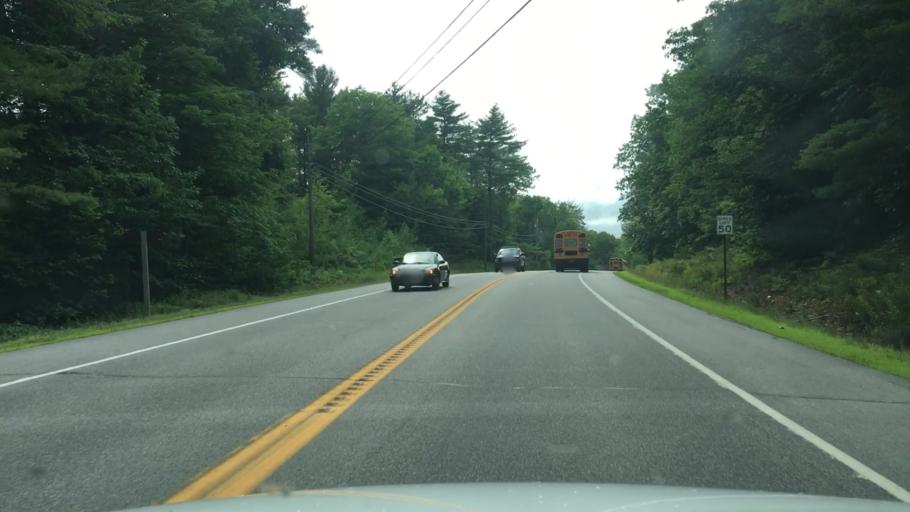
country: US
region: Maine
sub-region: Kennebec County
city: Chelsea
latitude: 44.2738
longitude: -69.6551
